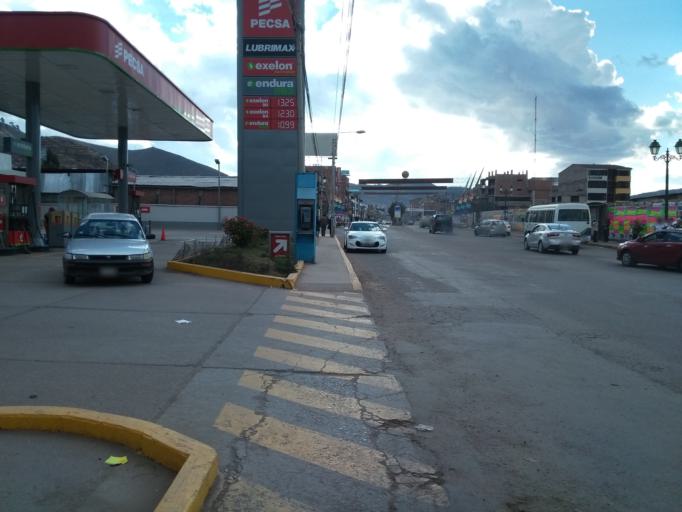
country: PE
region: Cusco
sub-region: Provincia de Cusco
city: Cusco
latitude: -13.5391
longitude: -71.9446
